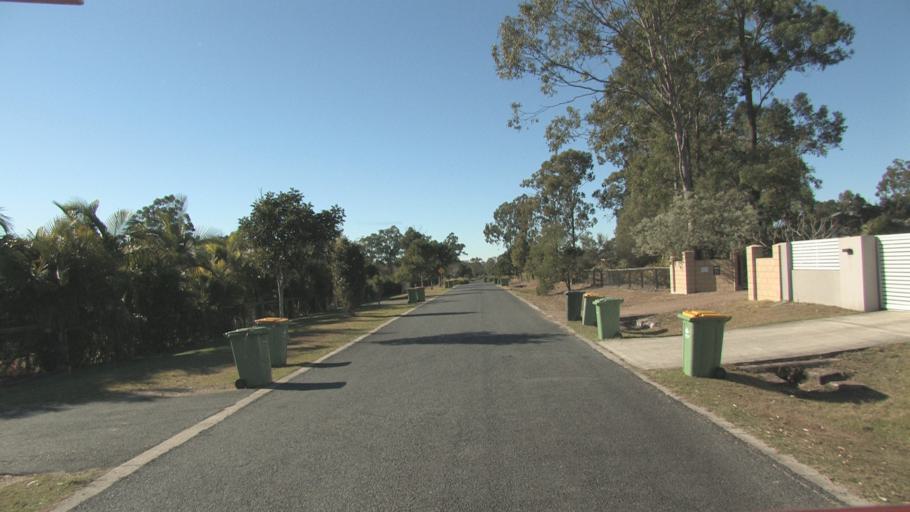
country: AU
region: Queensland
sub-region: Logan
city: North Maclean
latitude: -27.7473
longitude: 152.9605
